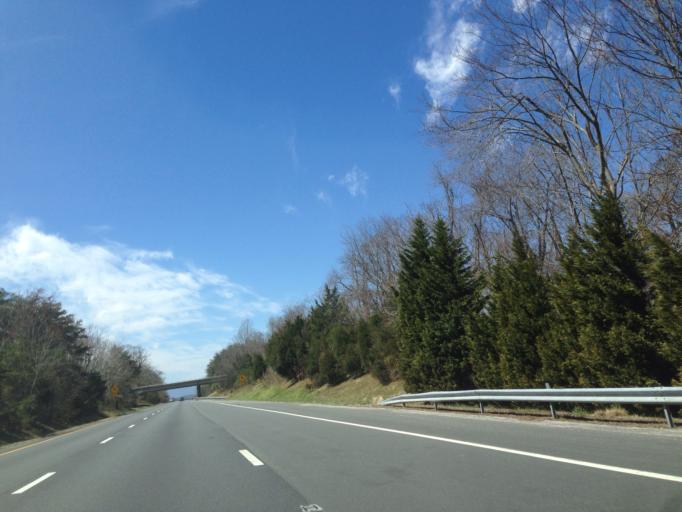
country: US
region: Virginia
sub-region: Albemarle County
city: Crozet
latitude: 38.0336
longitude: -78.6336
